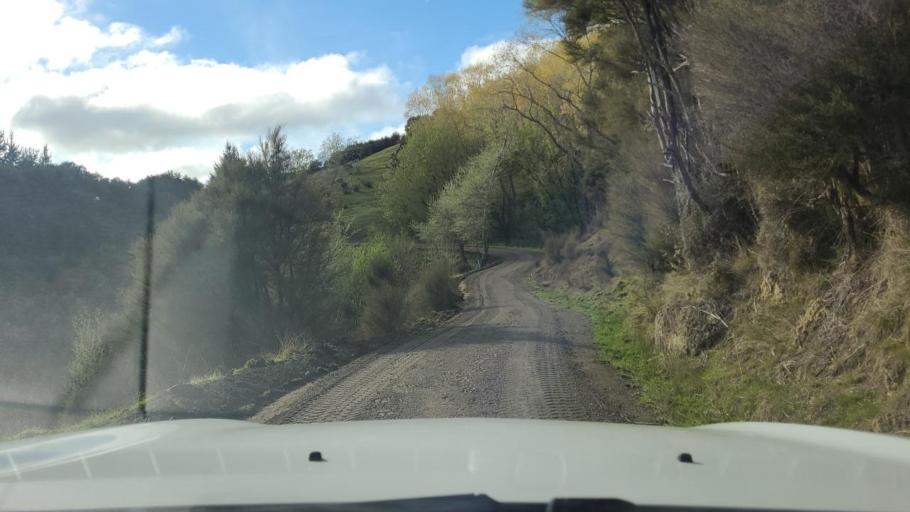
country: NZ
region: Wellington
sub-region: South Wairarapa District
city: Waipawa
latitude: -41.2400
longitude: 175.6981
